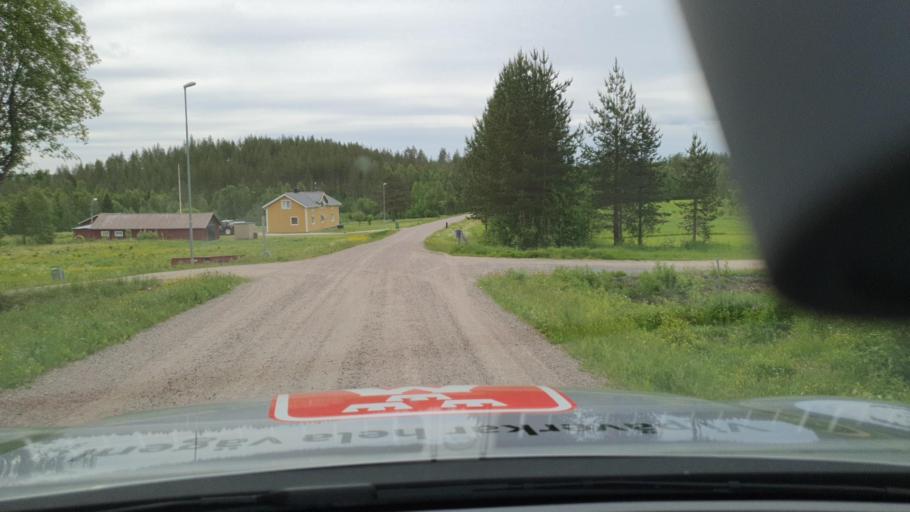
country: SE
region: Norrbotten
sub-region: Kalix Kommun
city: Kalix
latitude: 66.0232
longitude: 23.4418
